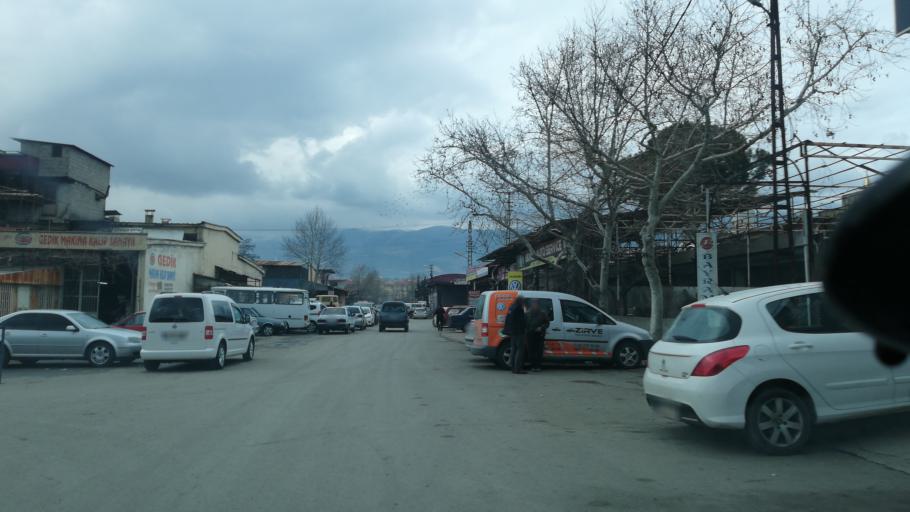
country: TR
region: Kahramanmaras
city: Kahramanmaras
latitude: 37.5646
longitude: 36.9596
